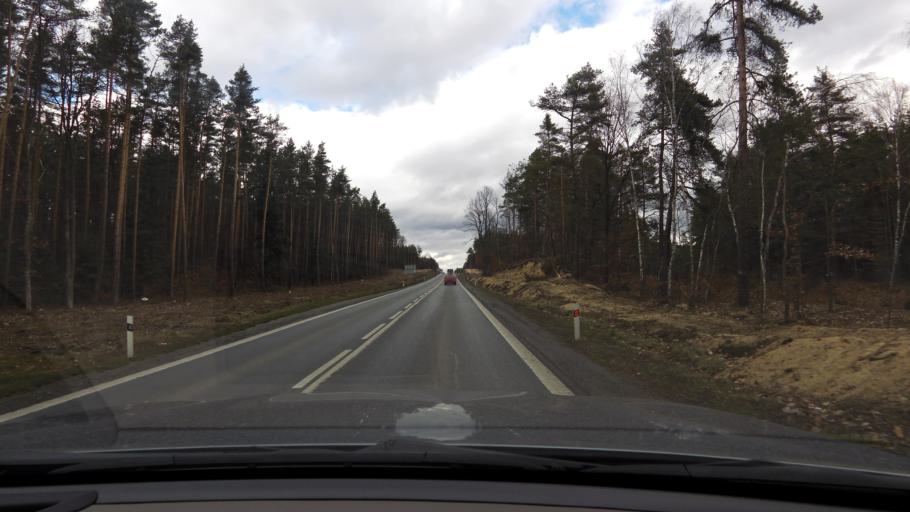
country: CZ
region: Plzensky
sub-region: Okres Plzen-Sever
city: Tremosna
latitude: 49.7918
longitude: 13.3849
